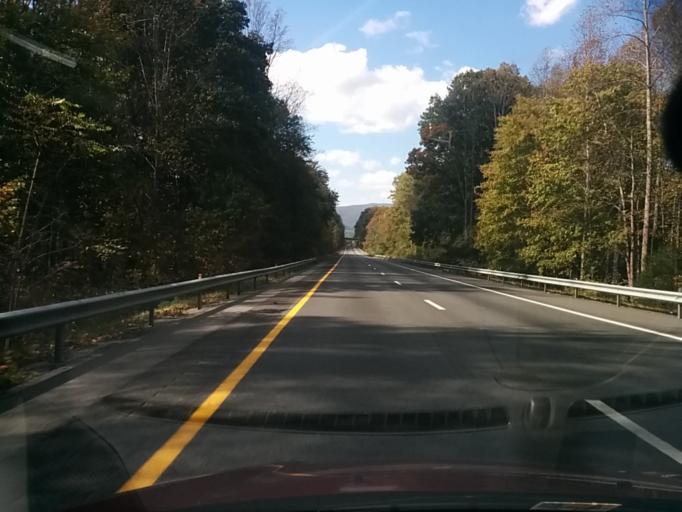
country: US
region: Virginia
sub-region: Albemarle County
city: Crozet
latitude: 38.0354
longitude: -78.6946
